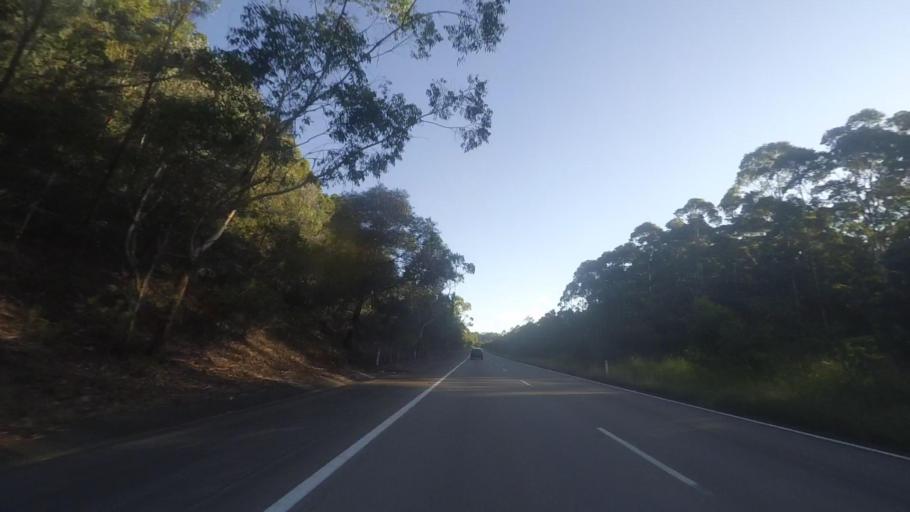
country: AU
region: New South Wales
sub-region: Great Lakes
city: Bulahdelah
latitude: -32.3085
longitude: 152.3449
